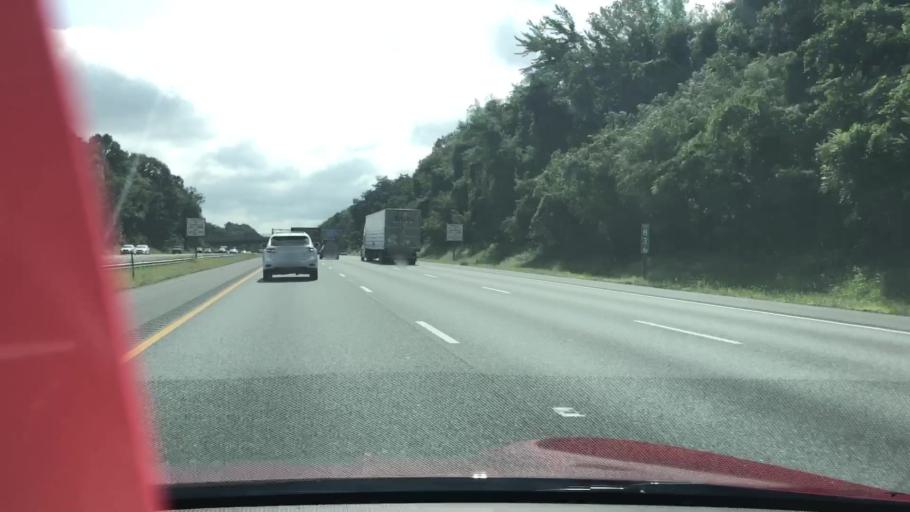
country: US
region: Maryland
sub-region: Harford County
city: Aberdeen
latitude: 39.5142
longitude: -76.2044
